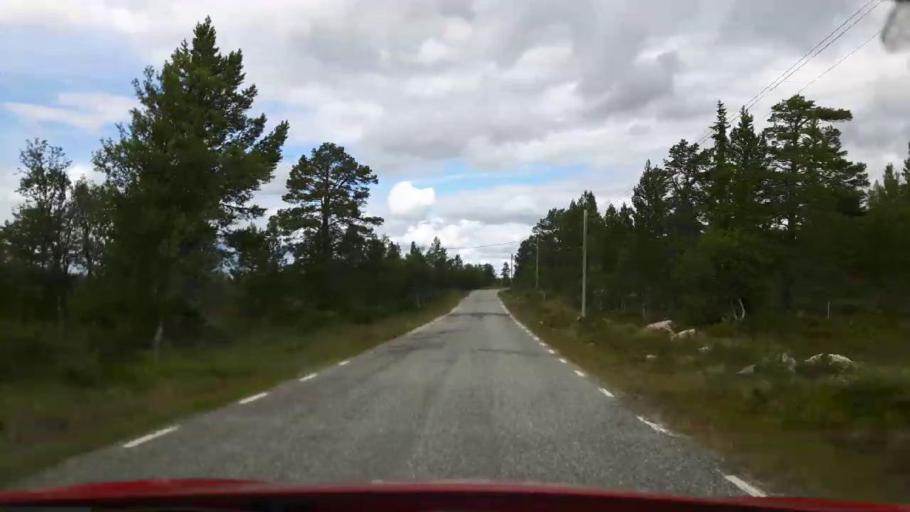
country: NO
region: Hedmark
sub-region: Engerdal
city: Engerdal
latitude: 62.3373
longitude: 12.7998
